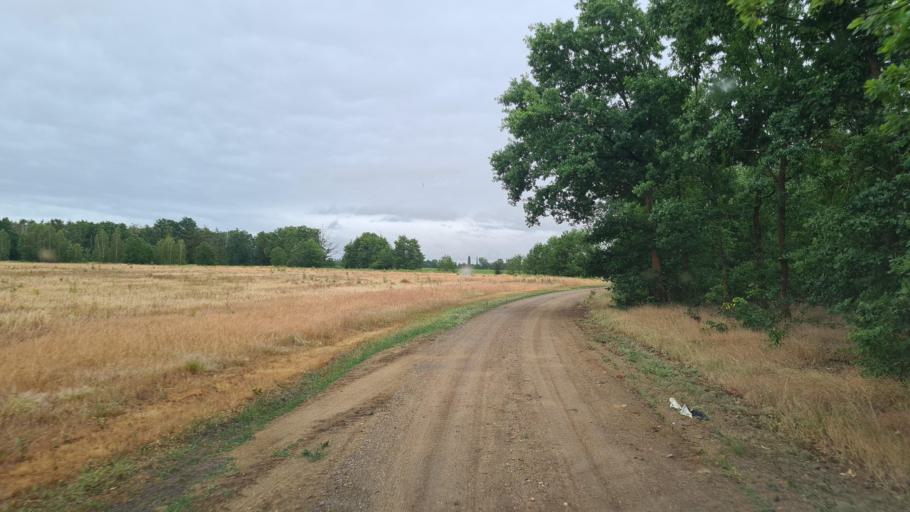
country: DE
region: Brandenburg
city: Bad Liebenwerda
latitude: 51.5023
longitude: 13.3173
